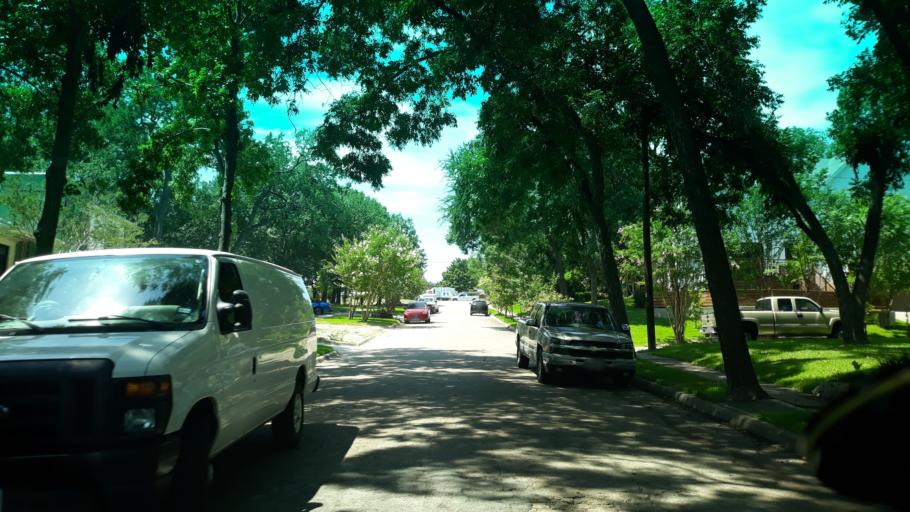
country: US
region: Texas
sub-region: Dallas County
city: Highland Park
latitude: 32.8152
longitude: -96.7338
